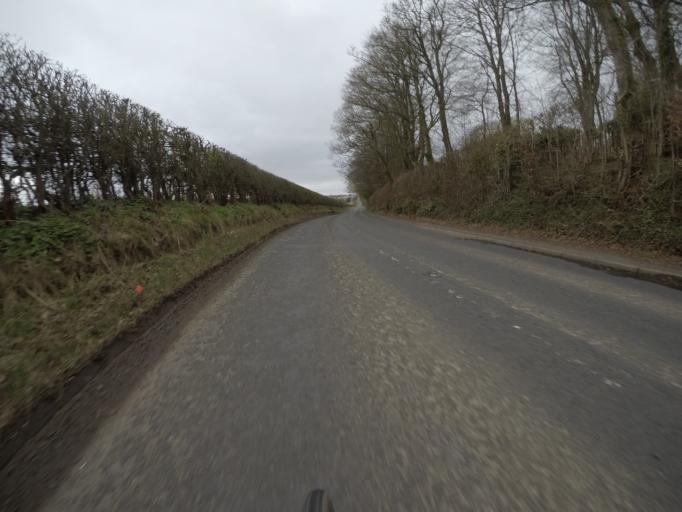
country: GB
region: Scotland
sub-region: North Ayrshire
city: Springside
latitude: 55.6114
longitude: -4.5761
